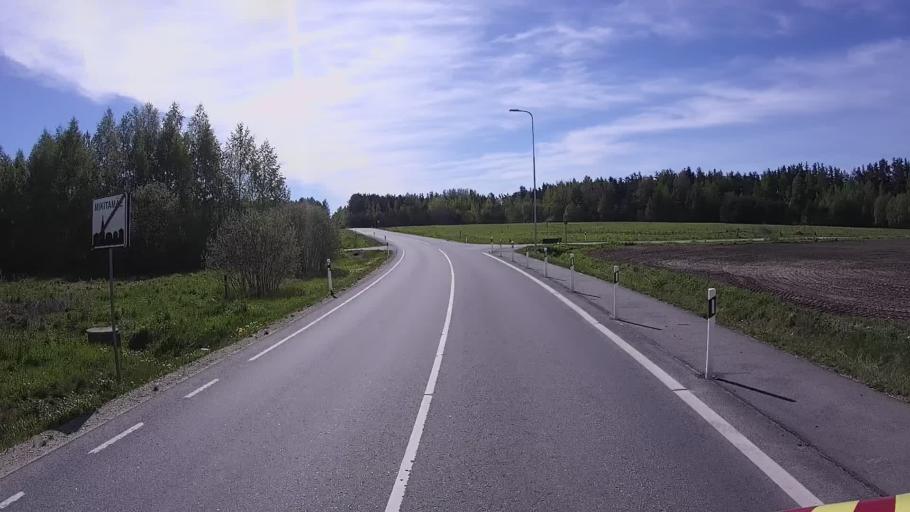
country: EE
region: Polvamaa
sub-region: Raepina vald
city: Rapina
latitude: 57.9996
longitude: 27.5451
